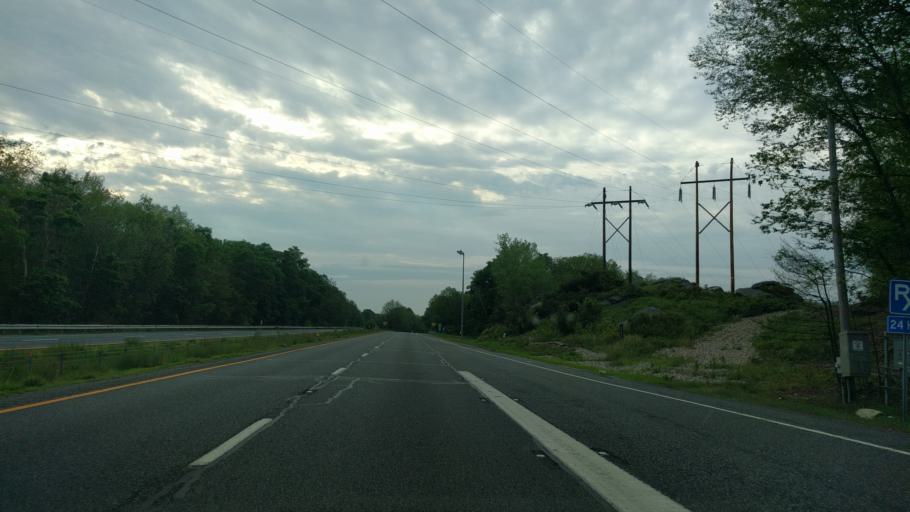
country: US
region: Rhode Island
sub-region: Providence County
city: Woonsocket
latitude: 41.9714
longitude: -71.5145
